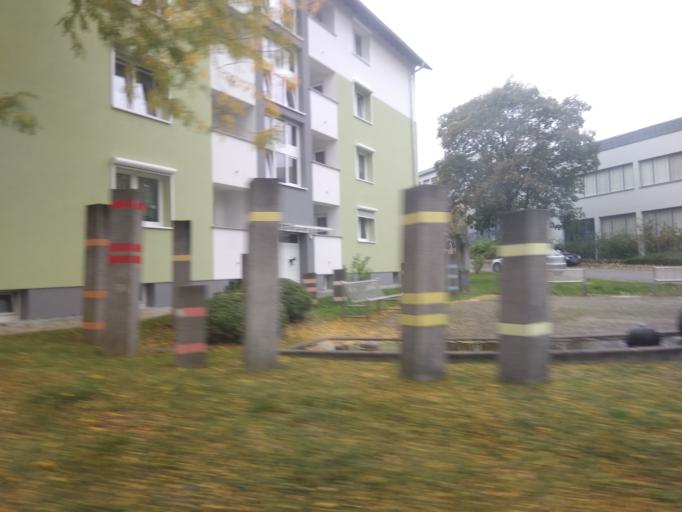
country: DE
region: Baden-Wuerttemberg
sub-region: Karlsruhe Region
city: Mosbach
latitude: 49.3541
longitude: 9.1521
